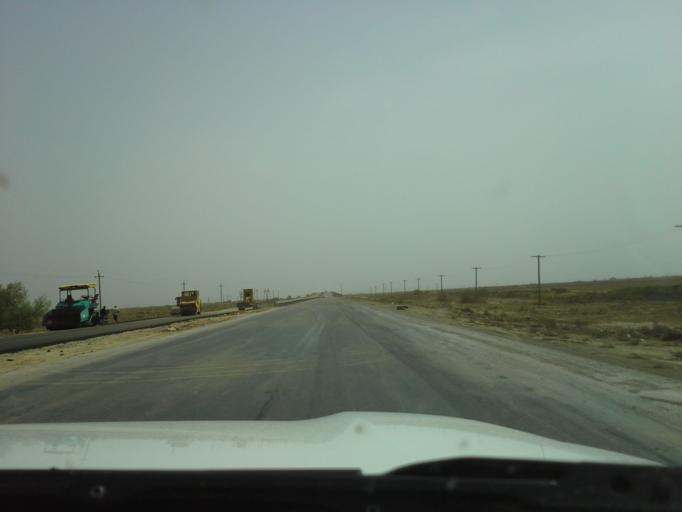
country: TM
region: Ahal
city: Tejen
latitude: 37.2276
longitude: 61.0469
